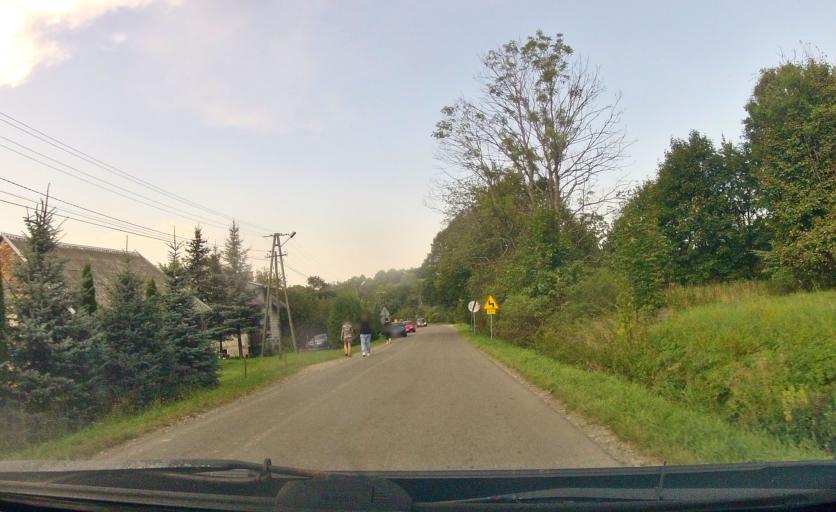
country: PL
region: Subcarpathian Voivodeship
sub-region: Powiat krosnienski
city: Dukla
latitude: 49.5458
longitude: 21.6217
